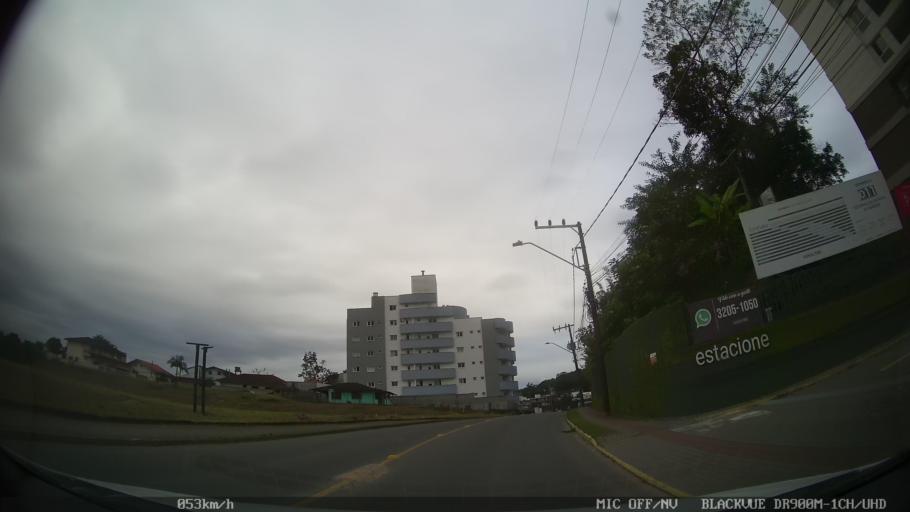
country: BR
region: Santa Catarina
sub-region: Joinville
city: Joinville
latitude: -26.2771
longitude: -48.8650
